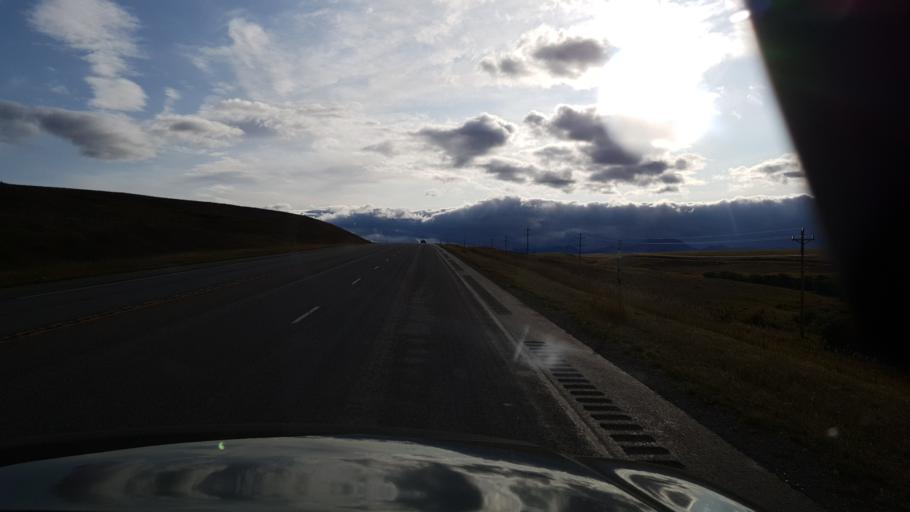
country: US
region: Montana
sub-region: Glacier County
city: South Browning
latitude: 48.5147
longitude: -113.0866
